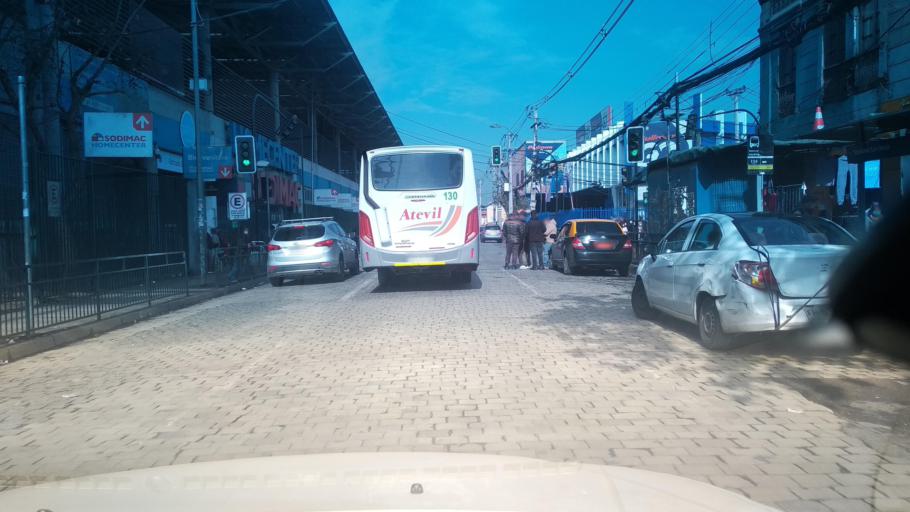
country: CL
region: Santiago Metropolitan
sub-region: Provincia de Santiago
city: Santiago
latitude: -33.4539
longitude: -70.6804
